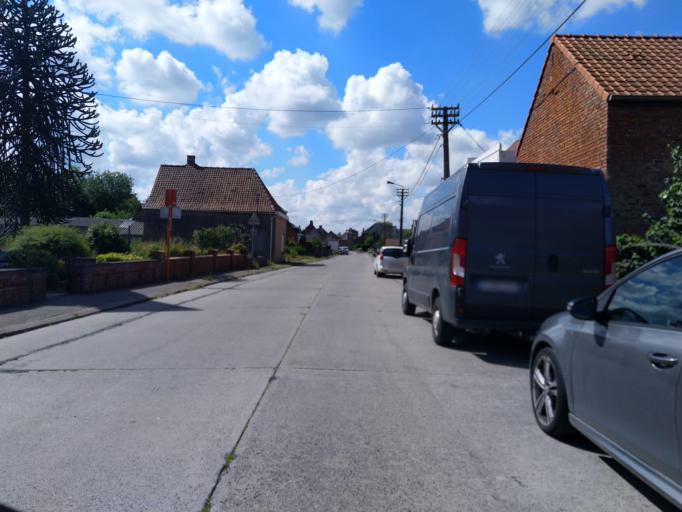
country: BE
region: Wallonia
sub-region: Province du Hainaut
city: Beloeil
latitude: 50.5897
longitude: 3.6870
